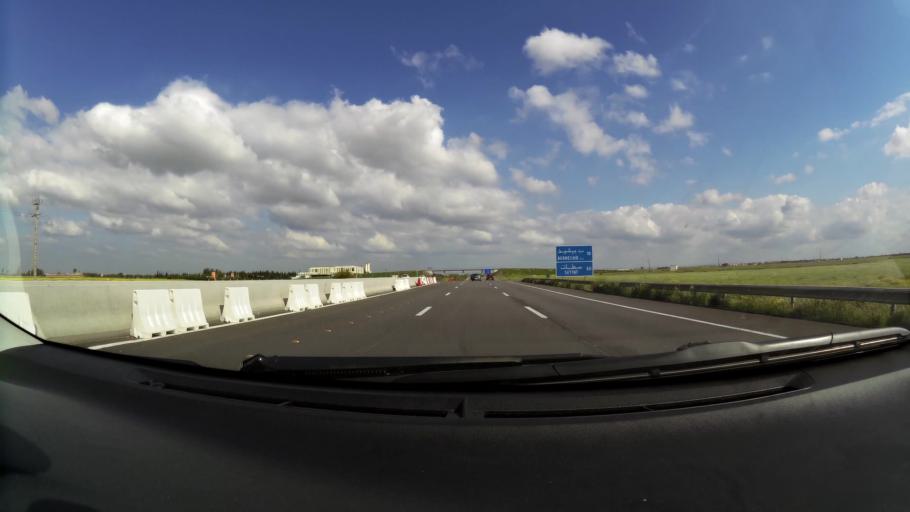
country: MA
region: Chaouia-Ouardigha
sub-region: Settat Province
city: Berrechid
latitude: 33.3143
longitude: -7.5981
